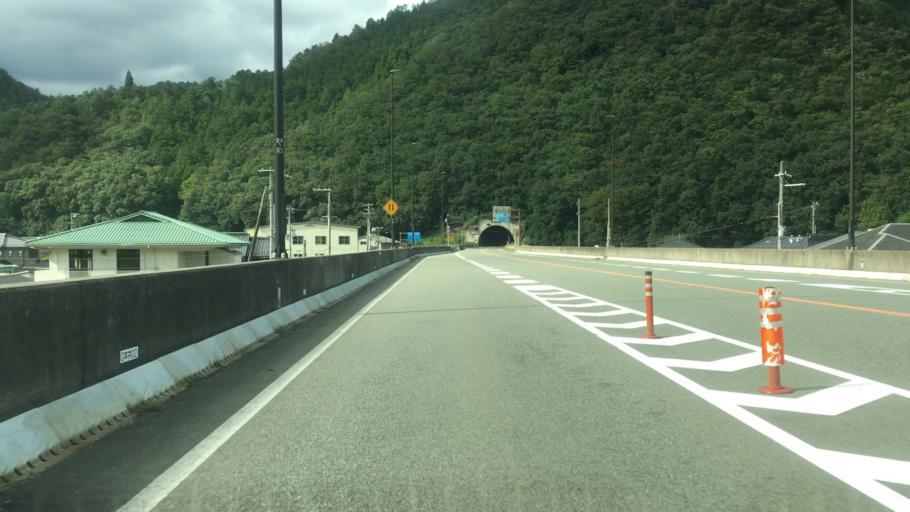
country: JP
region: Hyogo
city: Toyooka
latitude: 35.3827
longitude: 134.7793
